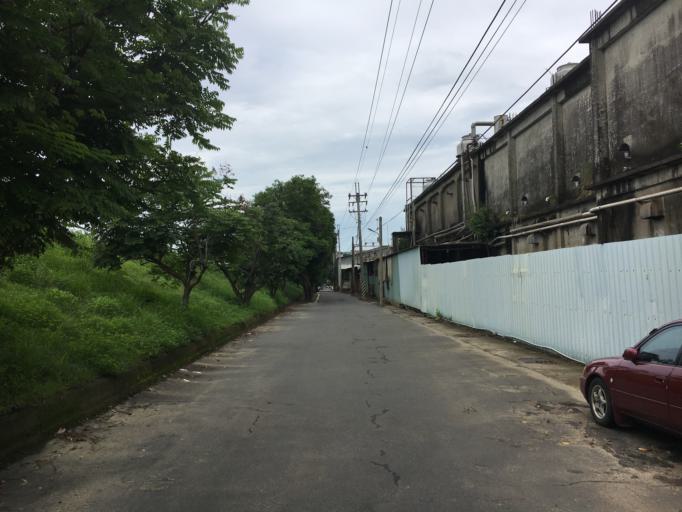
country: TW
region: Taiwan
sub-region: Taichung City
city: Taichung
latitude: 24.0850
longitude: 120.7185
